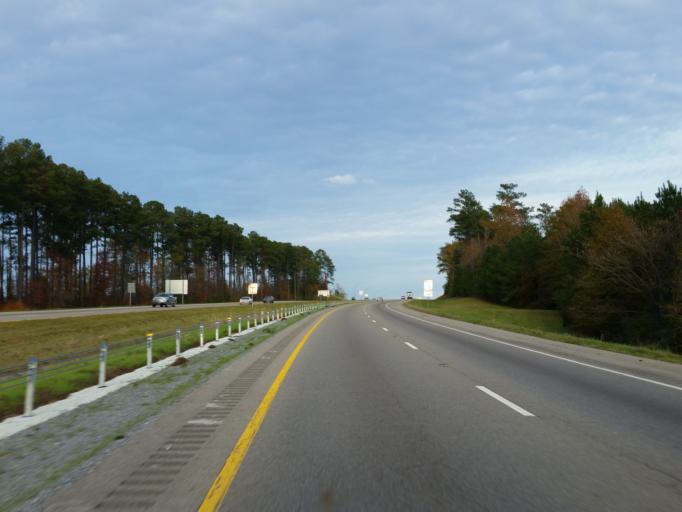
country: US
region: Mississippi
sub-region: Lauderdale County
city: Meridian
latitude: 32.3731
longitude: -88.6660
